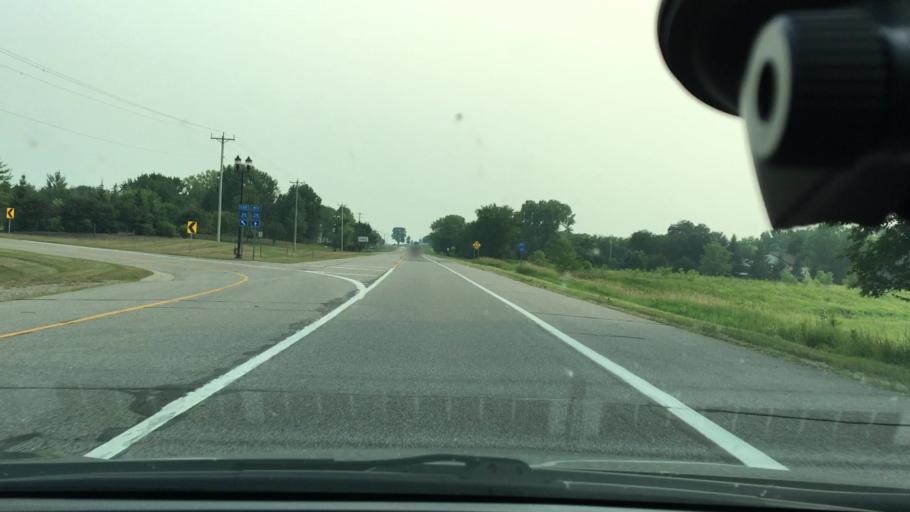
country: US
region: Minnesota
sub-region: Wright County
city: Saint Michael
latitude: 45.2086
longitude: -93.6761
